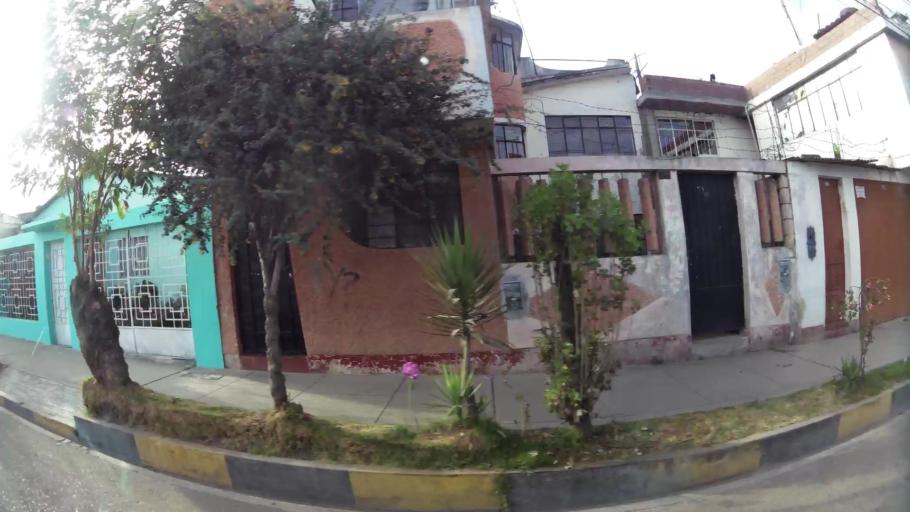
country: PE
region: Junin
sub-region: Provincia de Huancayo
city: Huancayo
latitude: -12.0495
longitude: -75.2008
